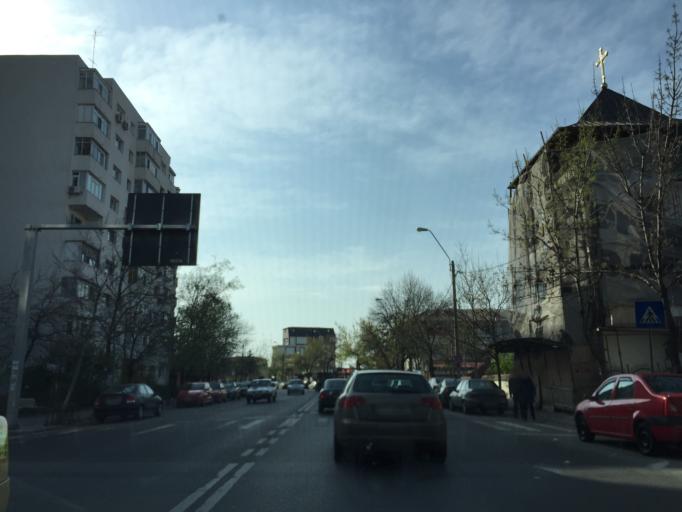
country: RO
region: Bucuresti
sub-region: Municipiul Bucuresti
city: Bucharest
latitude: 44.4140
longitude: 26.1333
